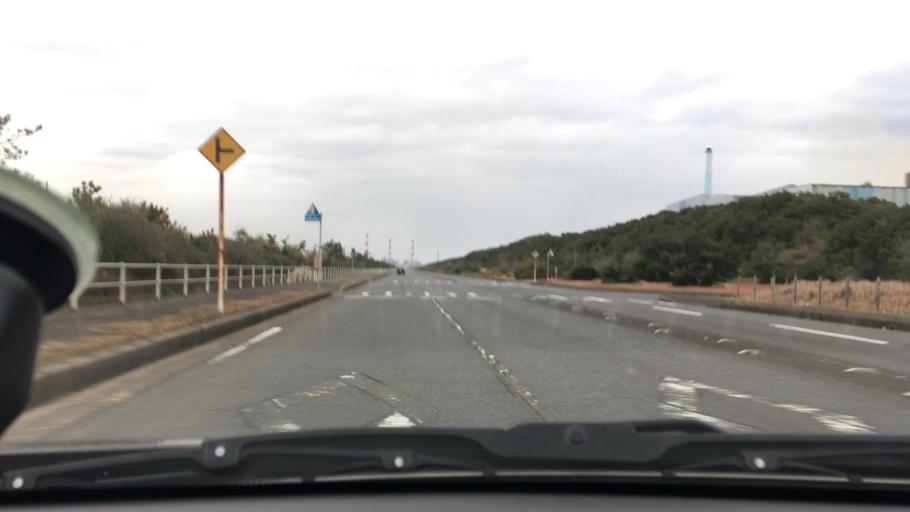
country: JP
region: Chiba
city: Omigawa
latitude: 35.8731
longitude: 140.7351
